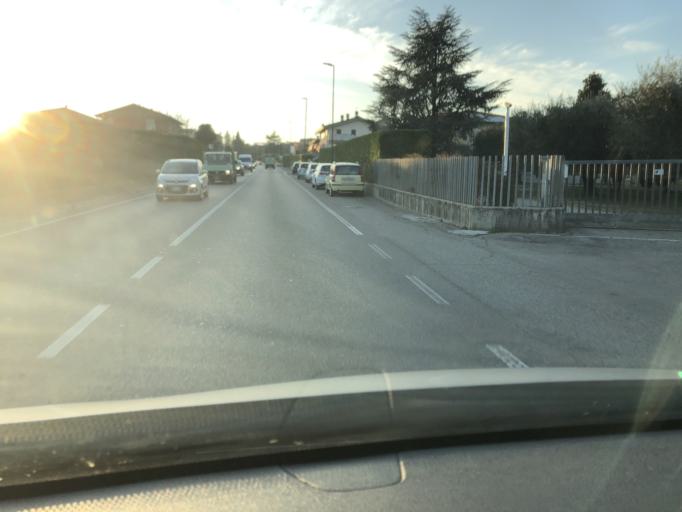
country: IT
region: Veneto
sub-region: Provincia di Verona
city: Bussolengo
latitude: 45.4774
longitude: 10.8267
